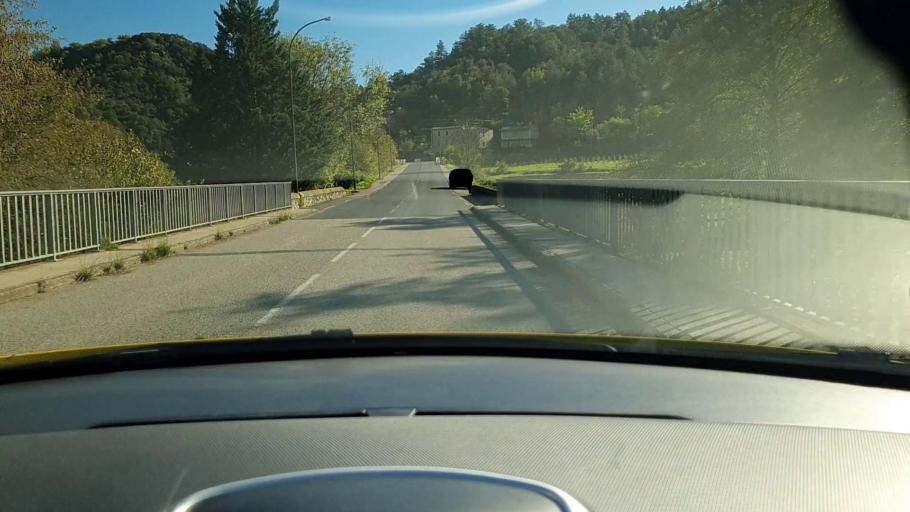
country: FR
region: Languedoc-Roussillon
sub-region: Departement du Gard
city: Le Vigan
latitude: 43.9902
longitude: 3.6095
